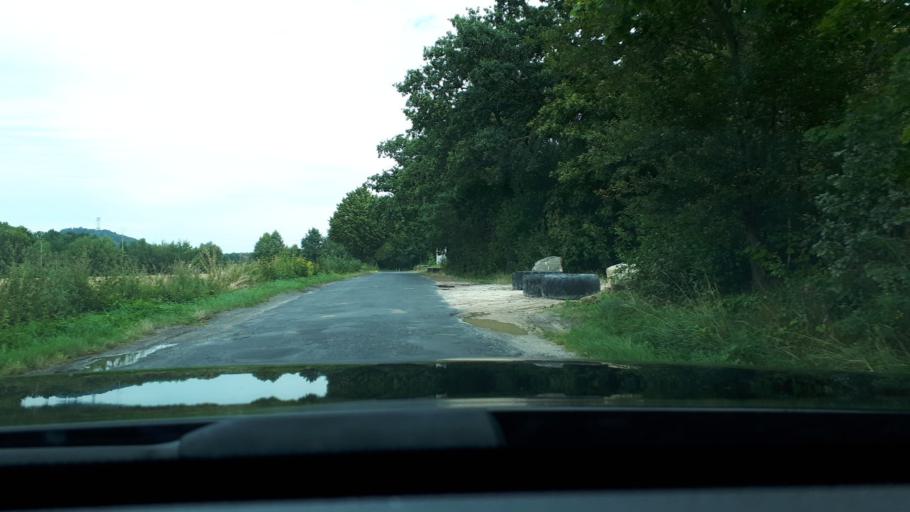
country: PL
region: Lower Silesian Voivodeship
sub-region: Powiat zlotoryjski
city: Olszanica
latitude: 51.1440
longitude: 15.7442
